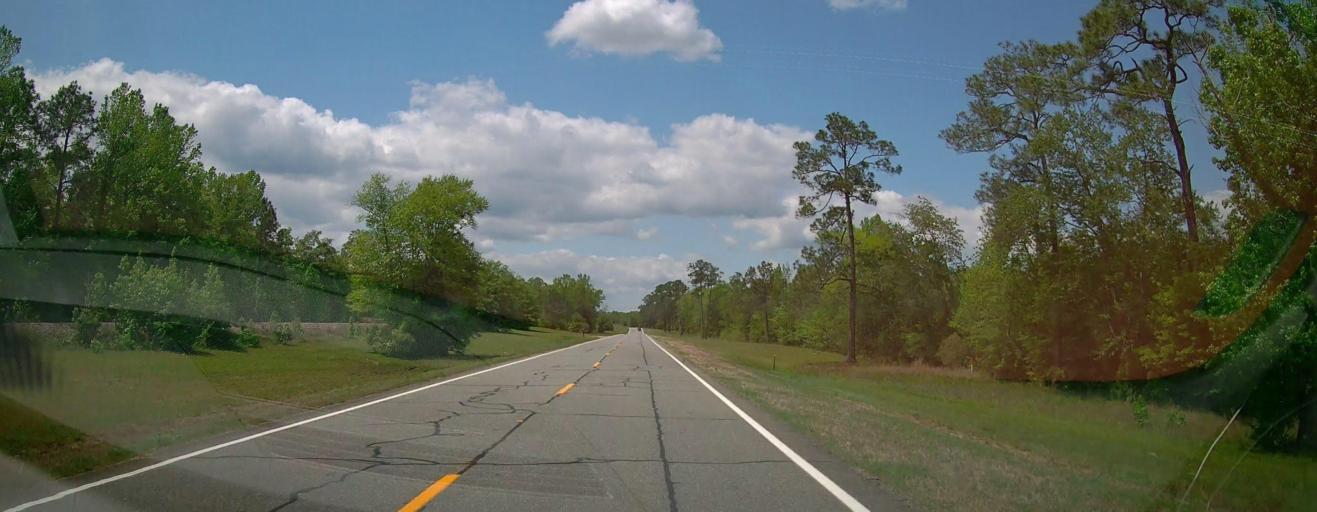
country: US
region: Georgia
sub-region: Treutlen County
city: Soperton
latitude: 32.4263
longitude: -82.6640
